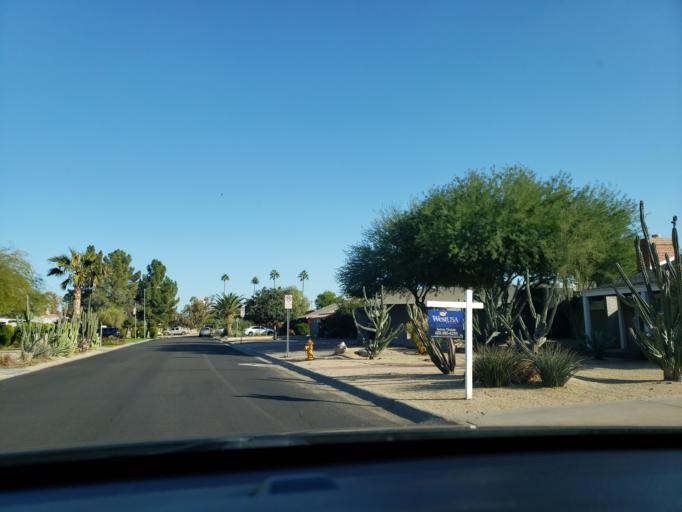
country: US
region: Arizona
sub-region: Maricopa County
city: Phoenix
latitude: 33.4793
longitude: -112.0546
